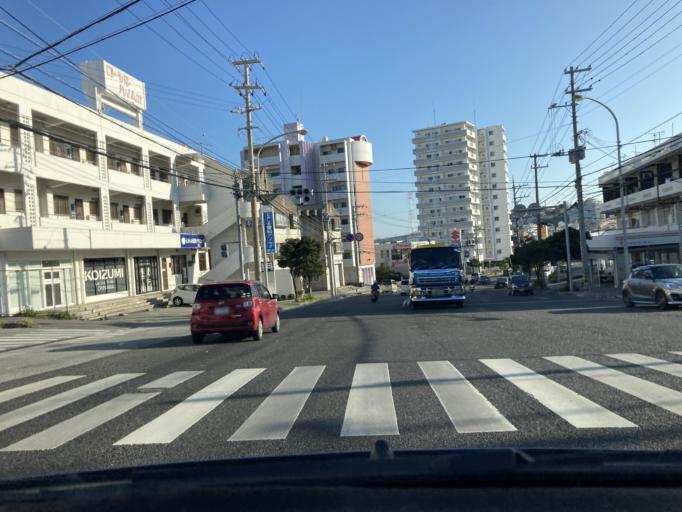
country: JP
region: Okinawa
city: Ginowan
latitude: 26.2508
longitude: 127.7388
